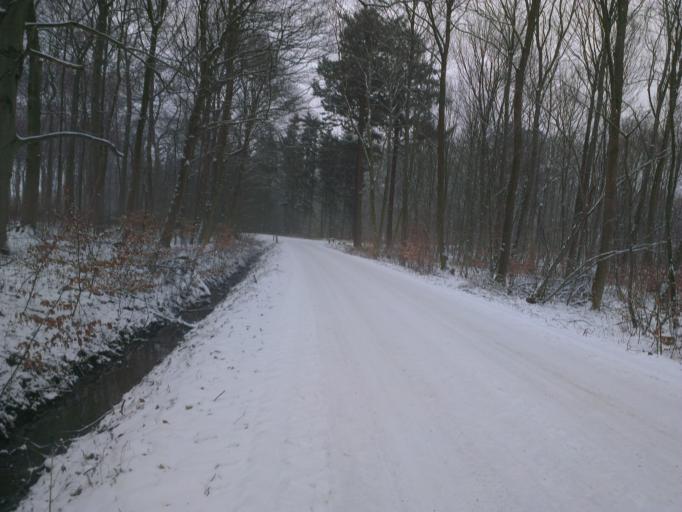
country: DK
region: Capital Region
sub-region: Frederikssund Kommune
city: Jaegerspris
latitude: 55.8745
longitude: 11.9847
